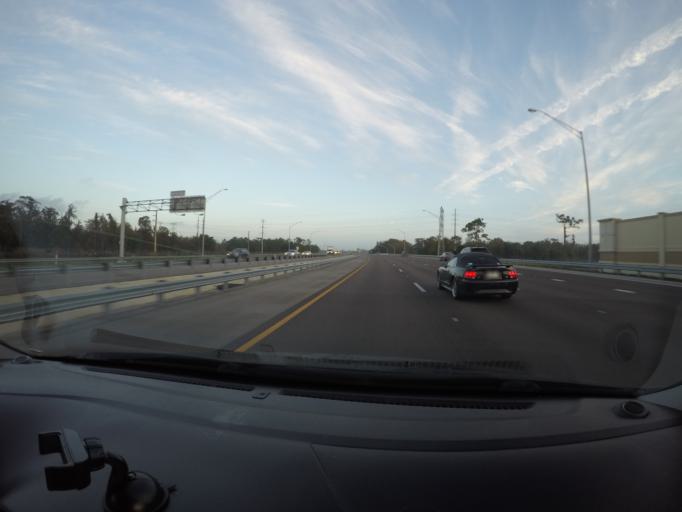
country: US
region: Florida
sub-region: Orange County
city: Azalea Park
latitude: 28.5007
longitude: -81.2437
